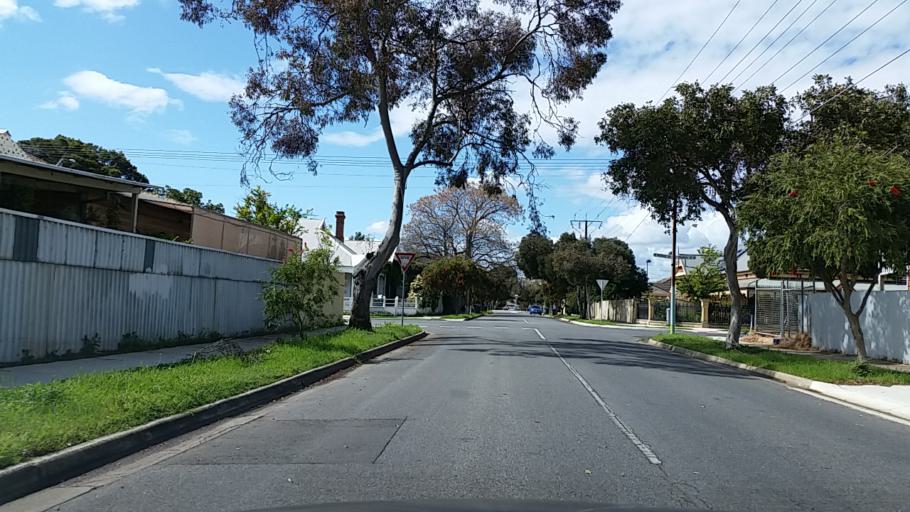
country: AU
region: South Australia
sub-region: Charles Sturt
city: Woodville
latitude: -34.8795
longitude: 138.5445
